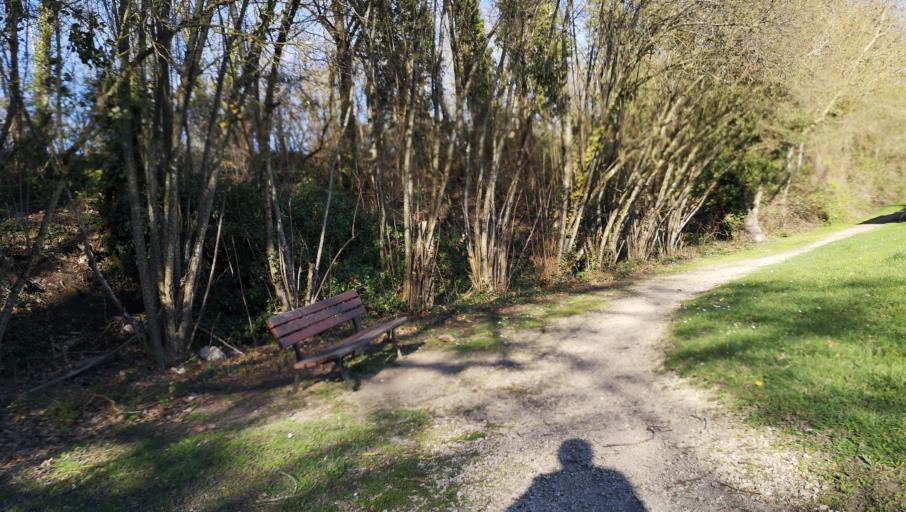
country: FR
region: Centre
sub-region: Departement du Loiret
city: Saint-Jean-de-Braye
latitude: 47.9102
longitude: 1.9903
